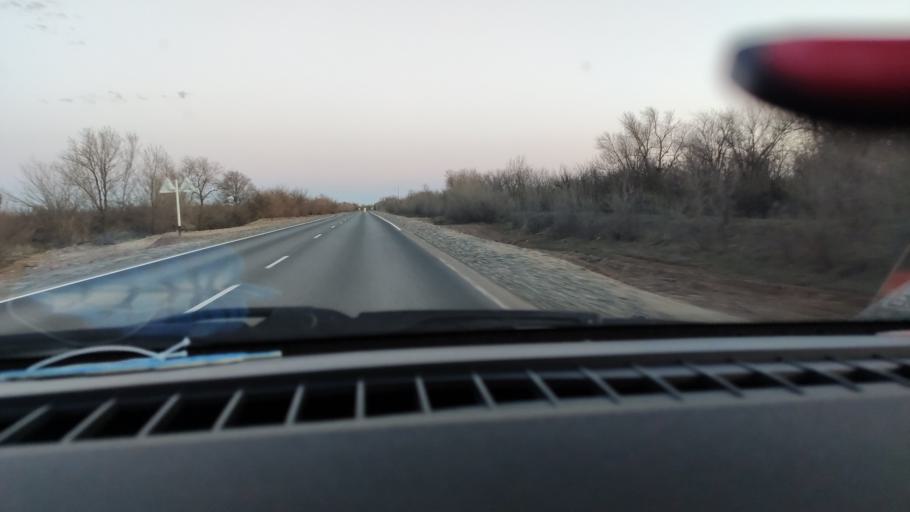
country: RU
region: Saratov
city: Krasnoarmeysk
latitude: 51.1126
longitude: 45.9576
